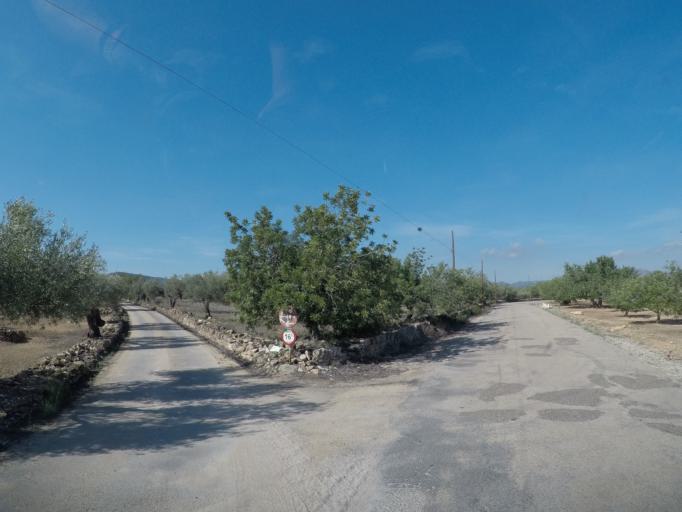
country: ES
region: Catalonia
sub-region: Provincia de Tarragona
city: El Perello
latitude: 40.8992
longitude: 0.7319
